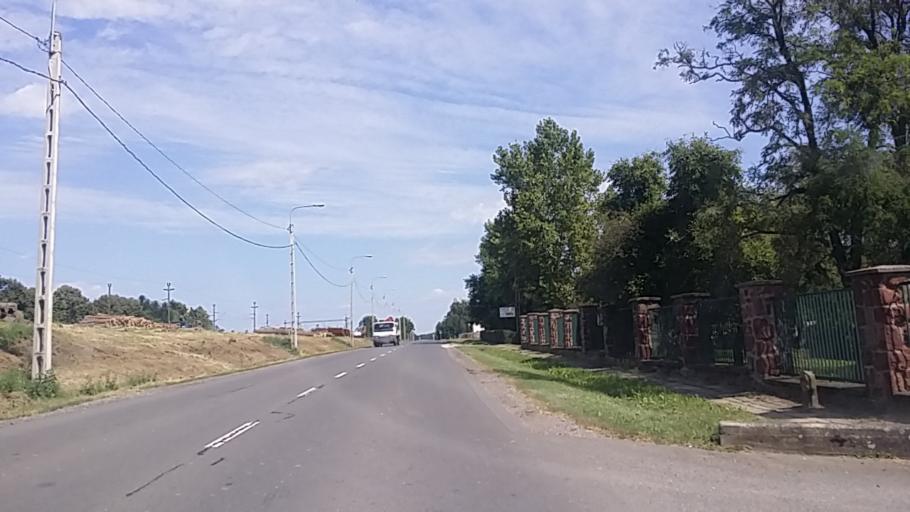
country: HU
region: Baranya
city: Sasd
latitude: 46.2592
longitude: 18.1054
